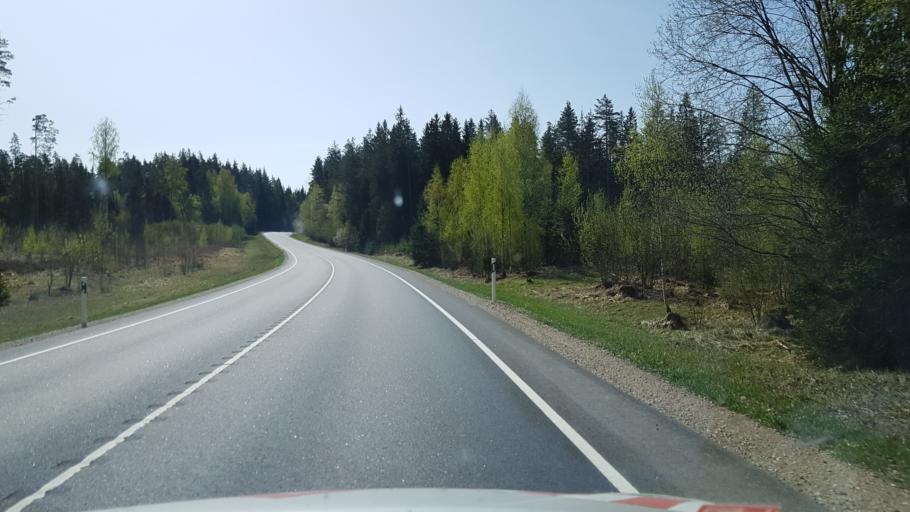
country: EE
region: Viljandimaa
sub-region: Karksi vald
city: Karksi-Nuia
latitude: 58.0491
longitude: 25.6415
